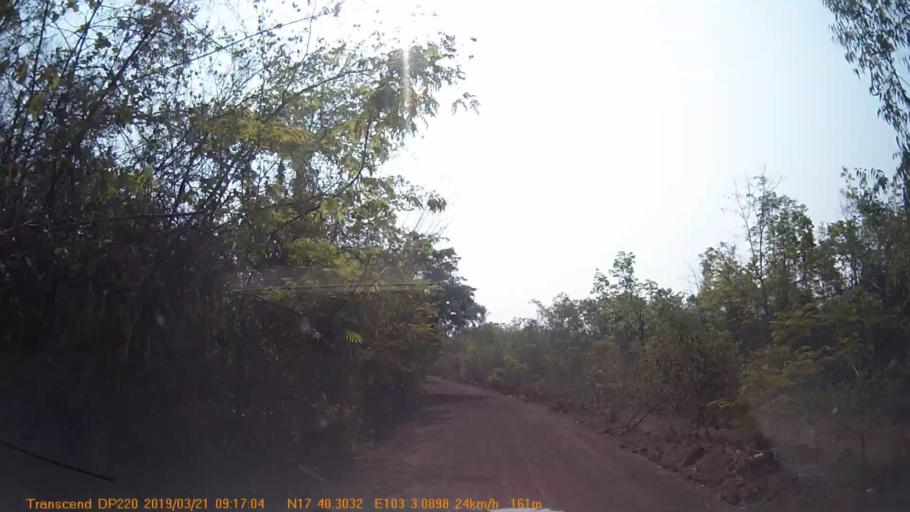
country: TH
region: Changwat Udon Thani
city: Phibun Rak
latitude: 17.6716
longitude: 103.0517
